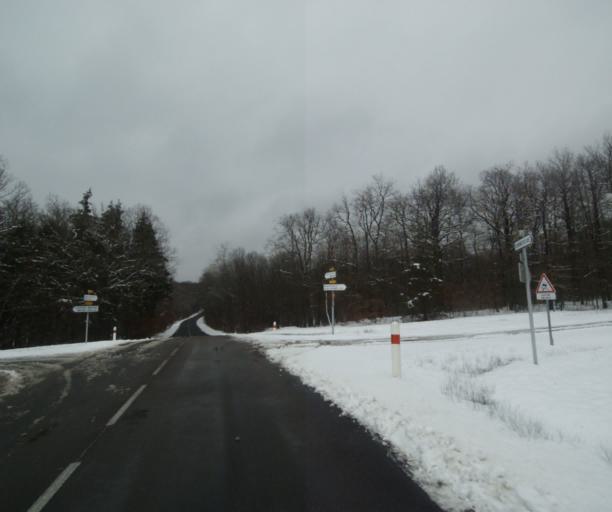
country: FR
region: Champagne-Ardenne
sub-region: Departement de la Haute-Marne
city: Laneuville-a-Remy
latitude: 48.4399
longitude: 4.8579
